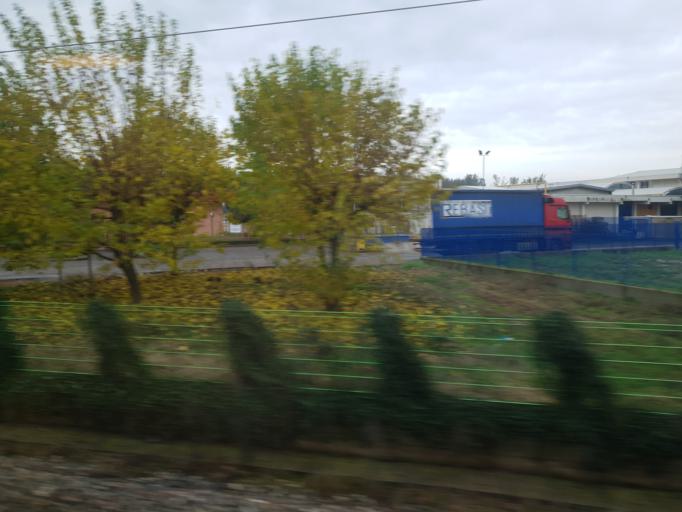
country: IT
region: Lombardy
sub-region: Citta metropolitana di Milano
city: Rescaldina
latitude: 45.6235
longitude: 8.9625
